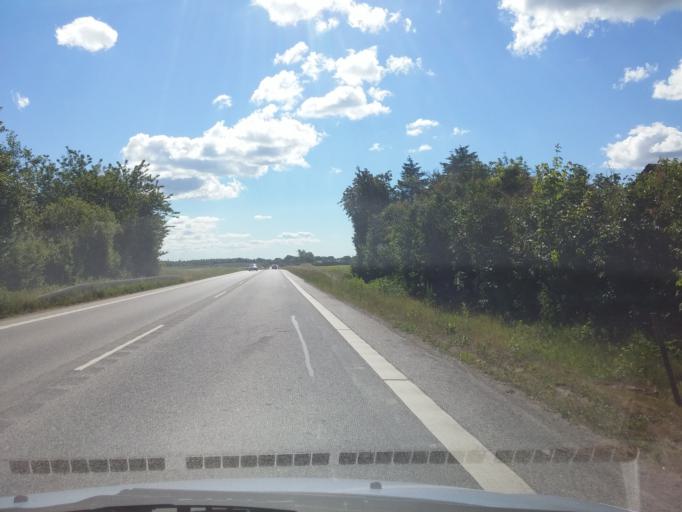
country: DK
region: South Denmark
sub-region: Haderslev Kommune
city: Haderslev
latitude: 55.2906
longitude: 9.4439
